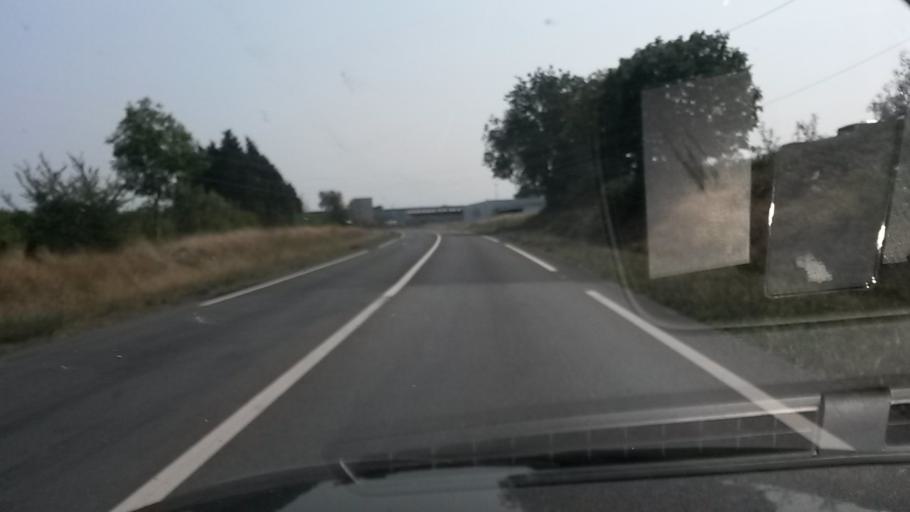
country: FR
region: Pays de la Loire
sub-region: Departement de la Loire-Atlantique
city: Ancenis
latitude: 47.3815
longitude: -1.1731
